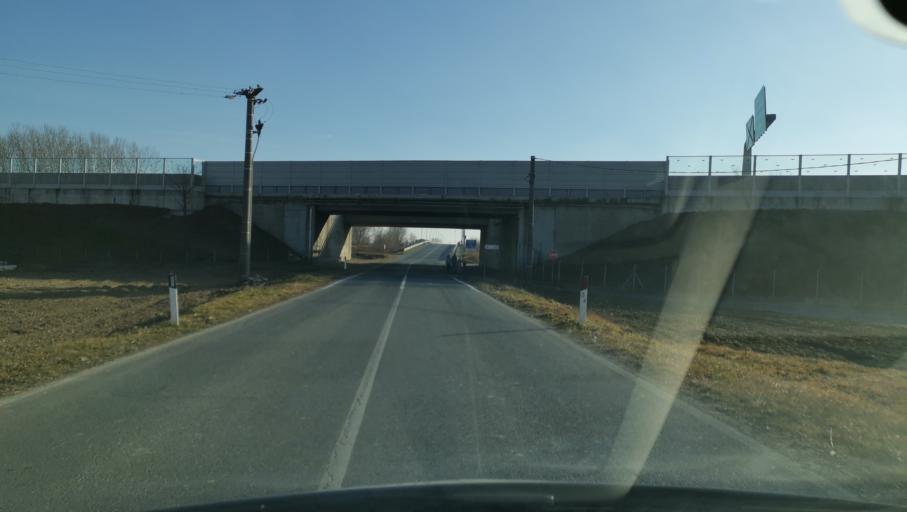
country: IT
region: Piedmont
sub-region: Provincia di Torino
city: Pavone Canavese
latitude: 45.4249
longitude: 7.8587
